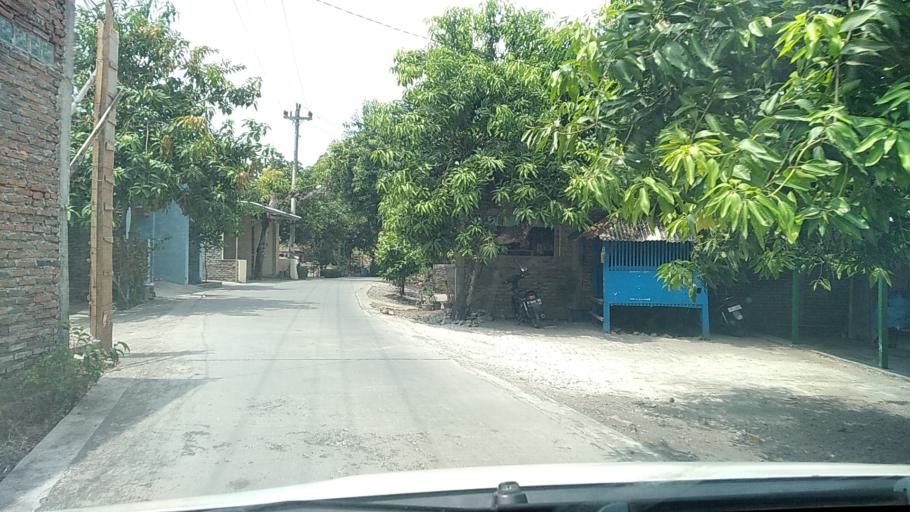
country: ID
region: Central Java
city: Mranggen
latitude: -7.0540
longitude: 110.4790
